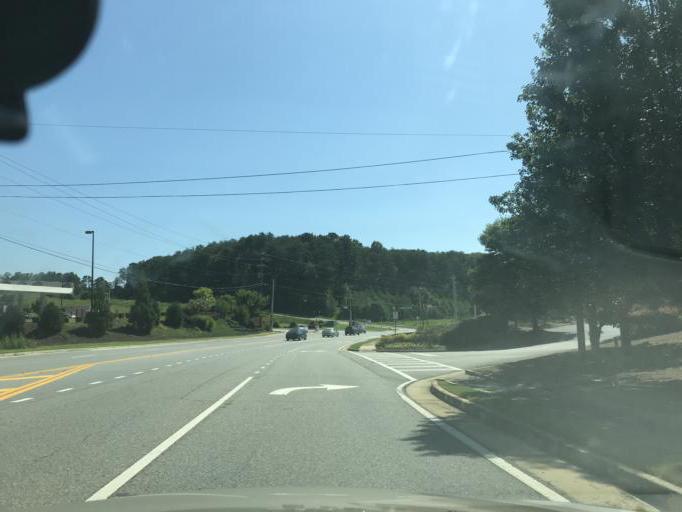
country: US
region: Georgia
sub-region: Forsyth County
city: Cumming
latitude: 34.2107
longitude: -84.1170
